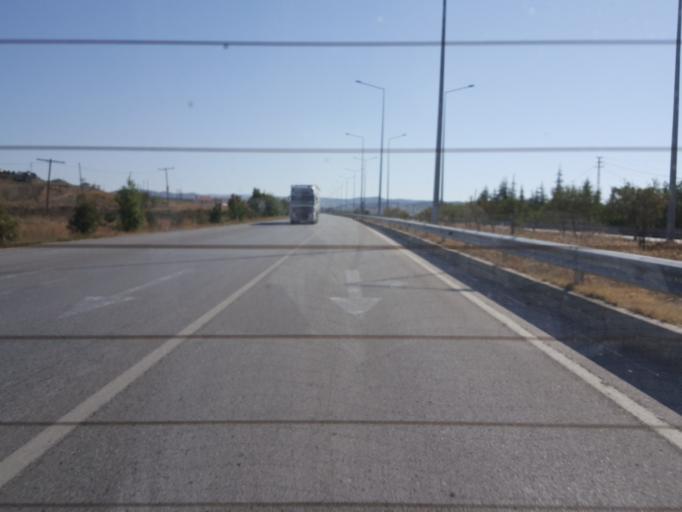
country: TR
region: Corum
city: Sungurlu
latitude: 40.1771
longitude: 34.4457
